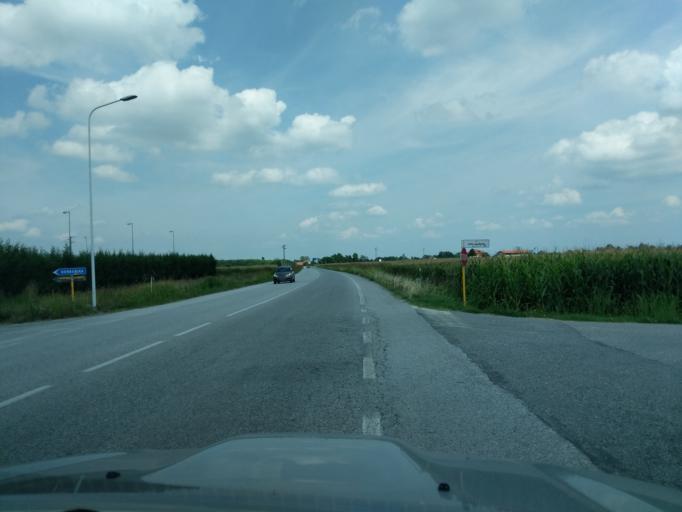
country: IT
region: Piedmont
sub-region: Provincia di Cuneo
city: Cuneo
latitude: 44.4098
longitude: 7.5929
